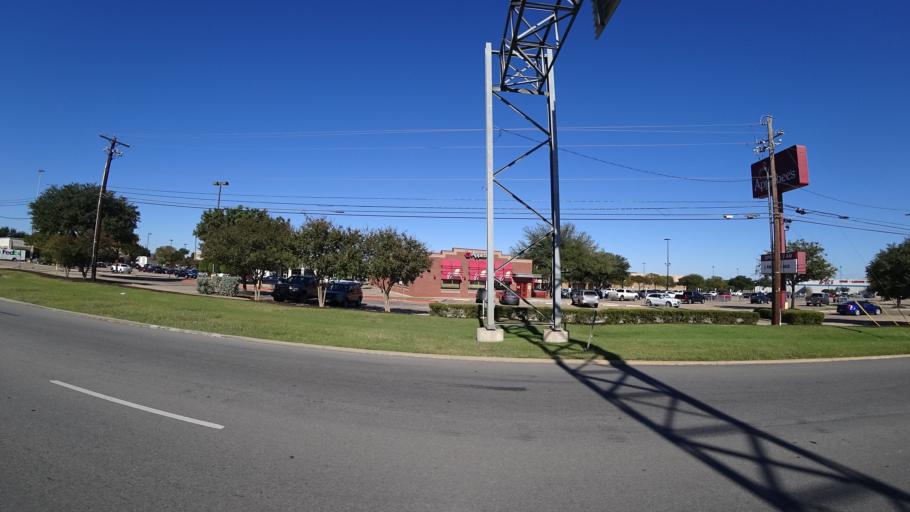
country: US
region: Texas
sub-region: Travis County
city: Rollingwood
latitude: 30.2347
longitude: -97.8214
